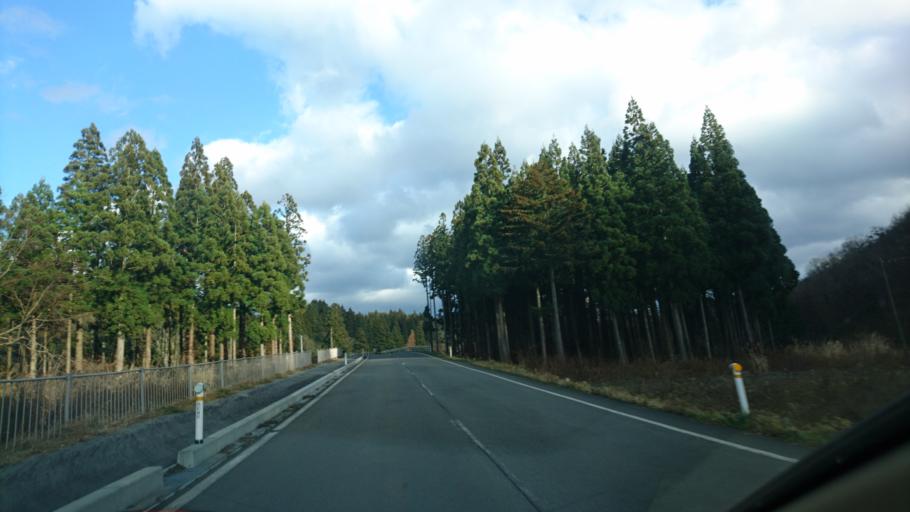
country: JP
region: Akita
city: Kakunodatemachi
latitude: 39.4501
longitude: 140.7818
